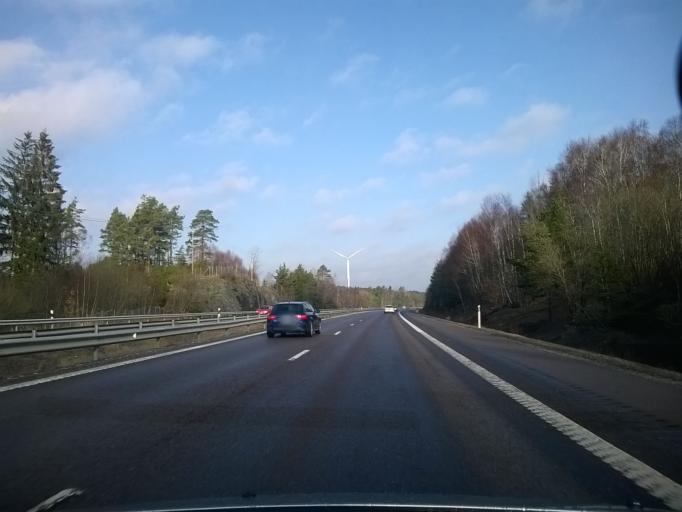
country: SE
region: Vaestra Goetaland
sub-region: Kungalvs Kommun
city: Kode
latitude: 57.9149
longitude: 11.8884
